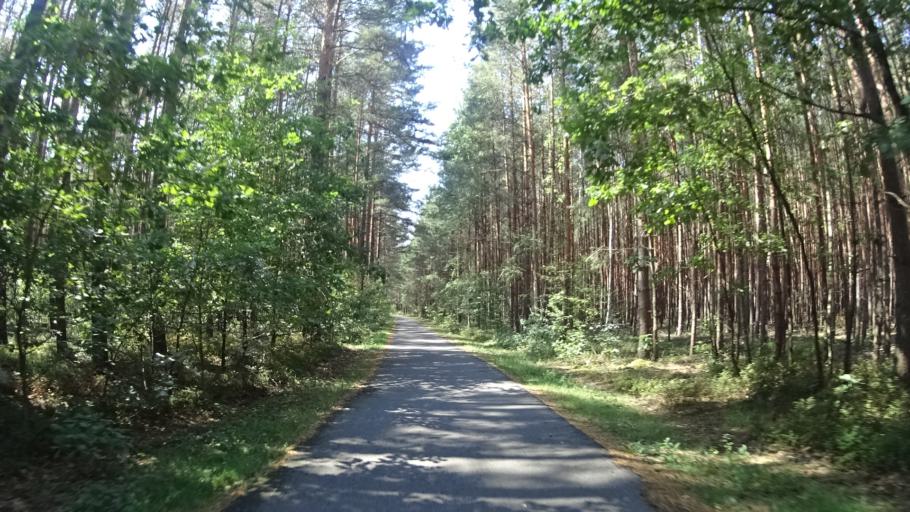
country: DE
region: Saxony
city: Gross Duben
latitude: 51.6087
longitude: 14.5390
